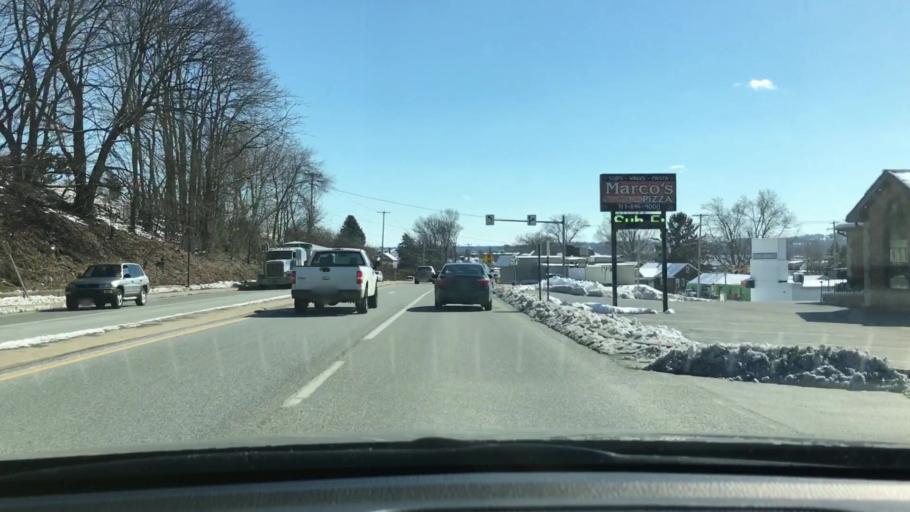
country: US
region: Pennsylvania
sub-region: York County
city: West York
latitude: 39.9616
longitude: -76.7611
